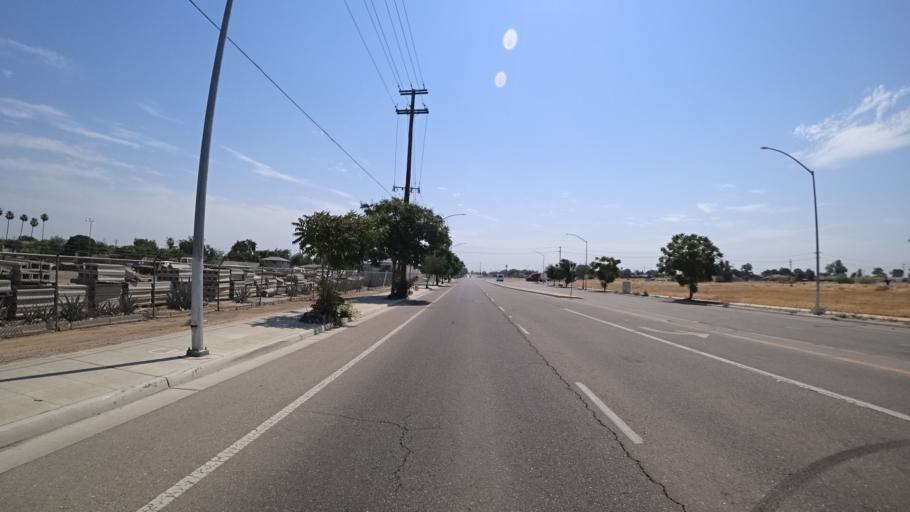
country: US
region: California
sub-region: Fresno County
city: West Park
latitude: 36.7214
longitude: -119.8193
